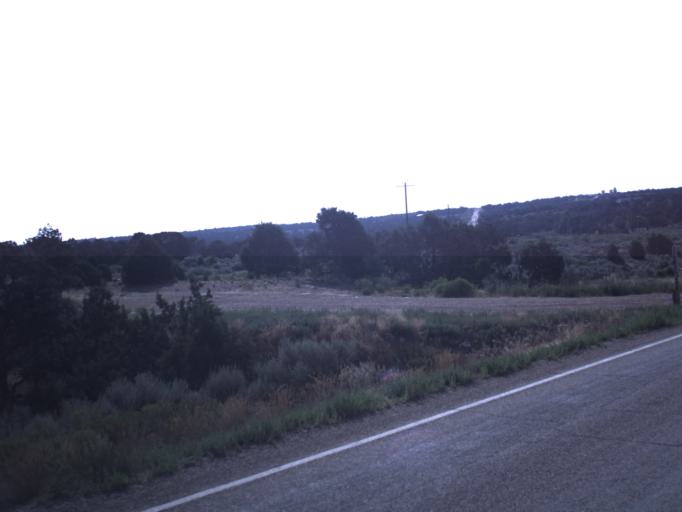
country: US
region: Utah
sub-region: Duchesne County
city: Duchesne
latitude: 40.3097
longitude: -110.3760
